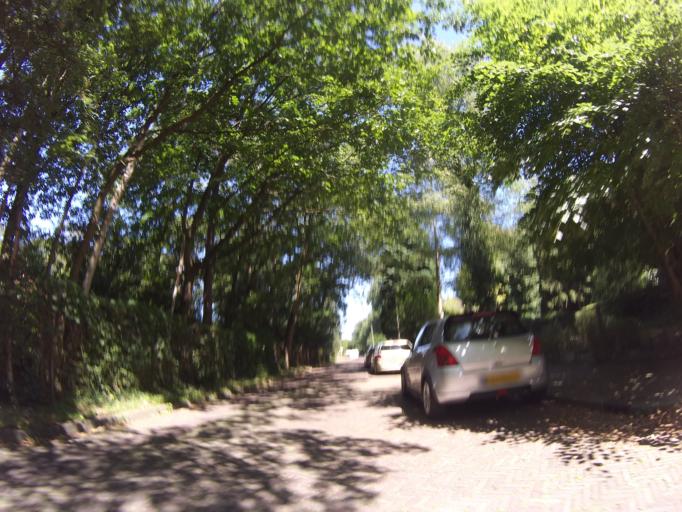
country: NL
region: Utrecht
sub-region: Gemeente Zeist
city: Zeist
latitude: 52.1388
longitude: 5.2443
